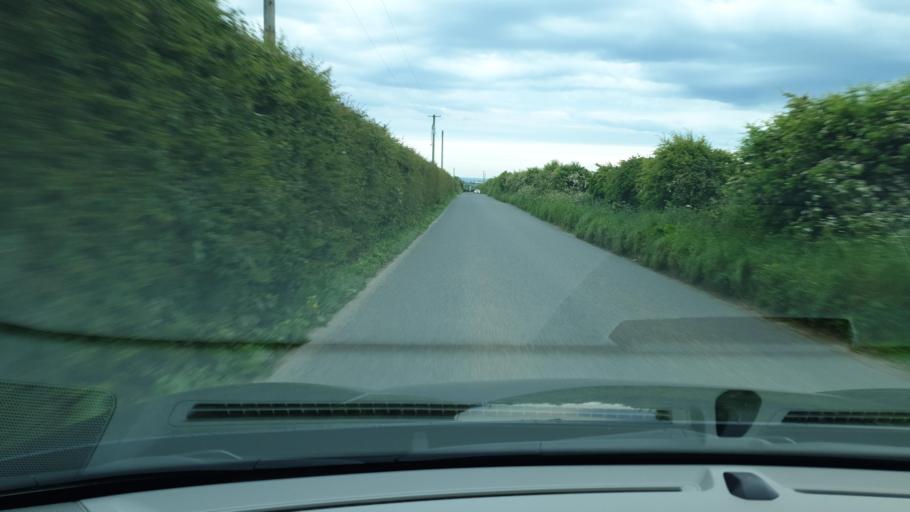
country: IE
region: Leinster
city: Lusk
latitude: 53.5551
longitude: -6.1579
